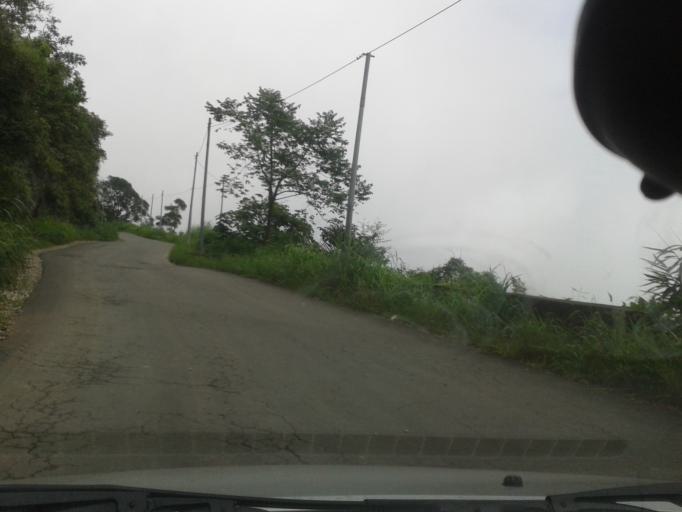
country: IN
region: Meghalaya
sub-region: East Khasi Hills
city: Cherrapunji
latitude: 25.2077
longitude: 91.7397
